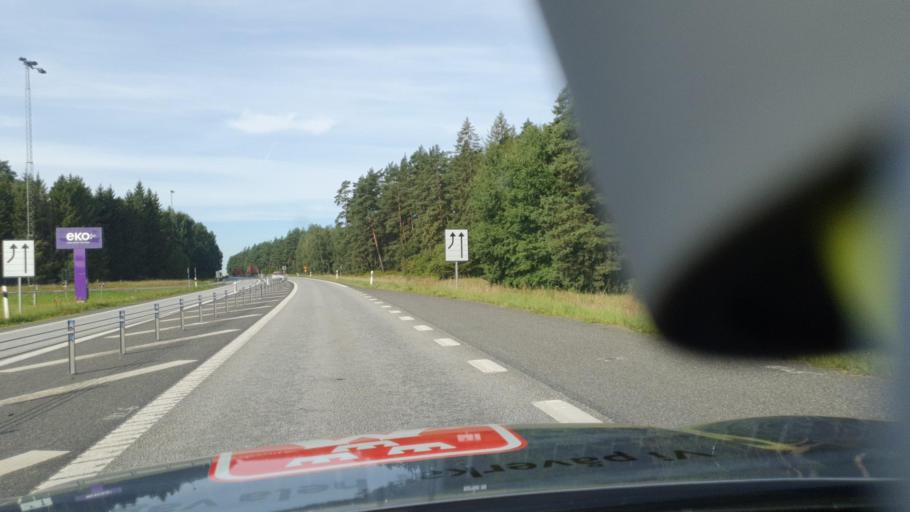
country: SE
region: Skane
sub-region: Kristianstads Kommun
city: Fjalkinge
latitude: 56.0412
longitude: 14.3113
